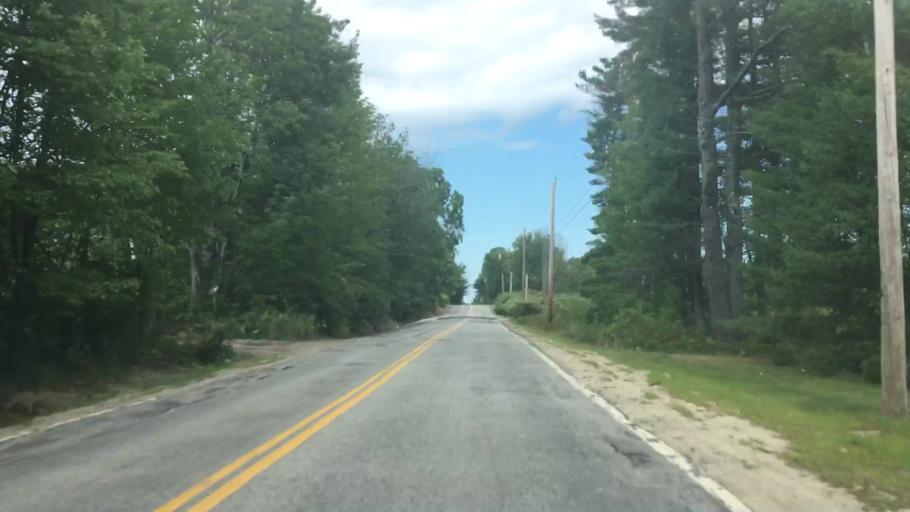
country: US
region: Maine
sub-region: Oxford County
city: Oxford
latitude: 44.0794
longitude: -70.5482
